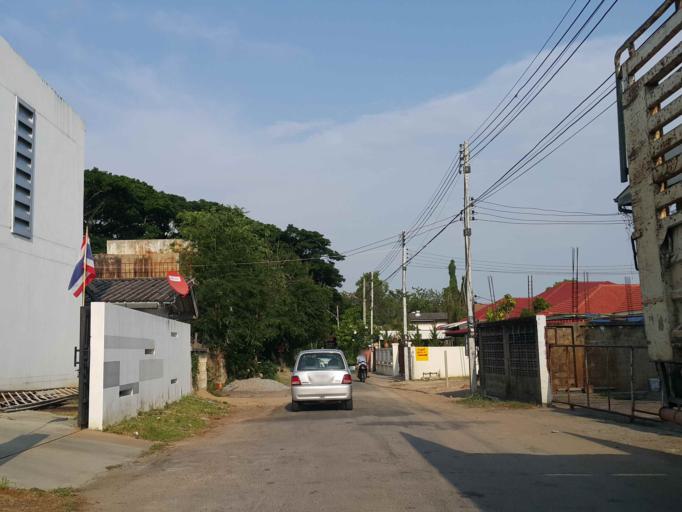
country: TH
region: Chiang Mai
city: Chiang Mai
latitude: 18.7754
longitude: 99.0218
